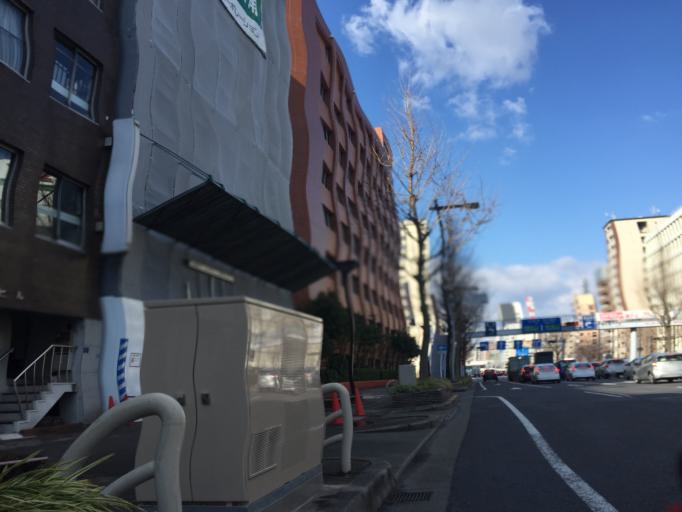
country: JP
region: Aichi
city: Nagoya-shi
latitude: 35.1741
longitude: 136.9223
